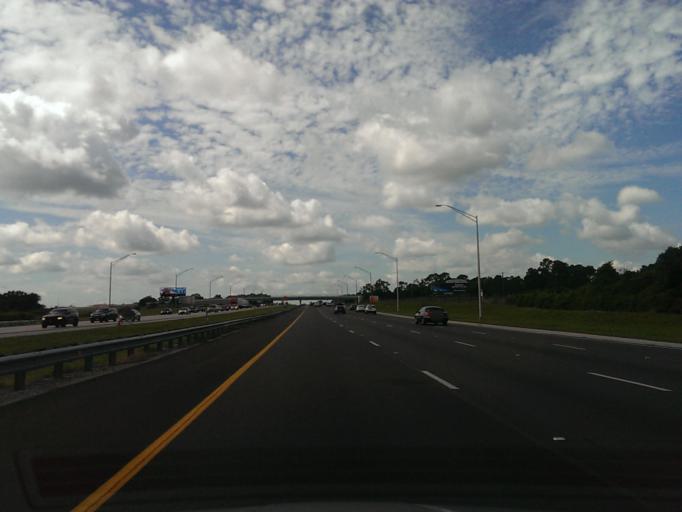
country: US
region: Florida
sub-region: Orange County
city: Williamsburg
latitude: 28.4017
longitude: -81.4830
